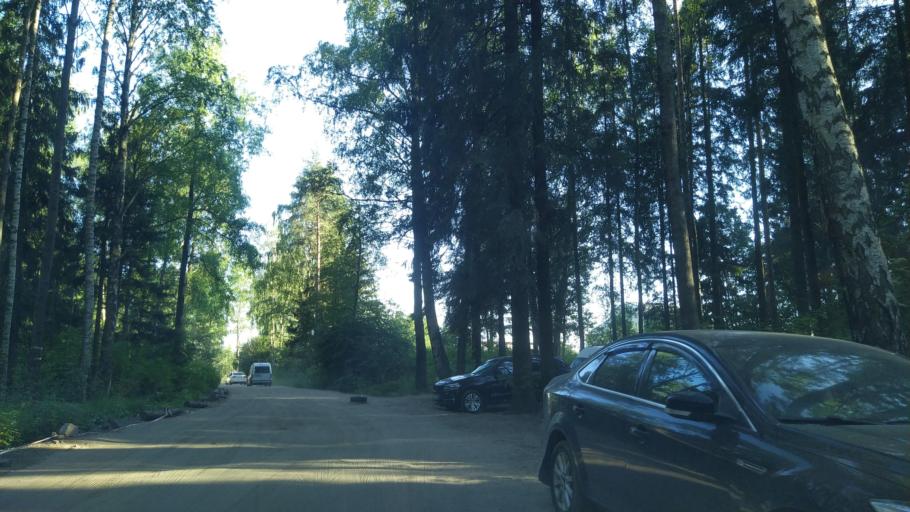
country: RU
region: Leningrad
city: Koltushi
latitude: 59.9165
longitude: 30.7348
